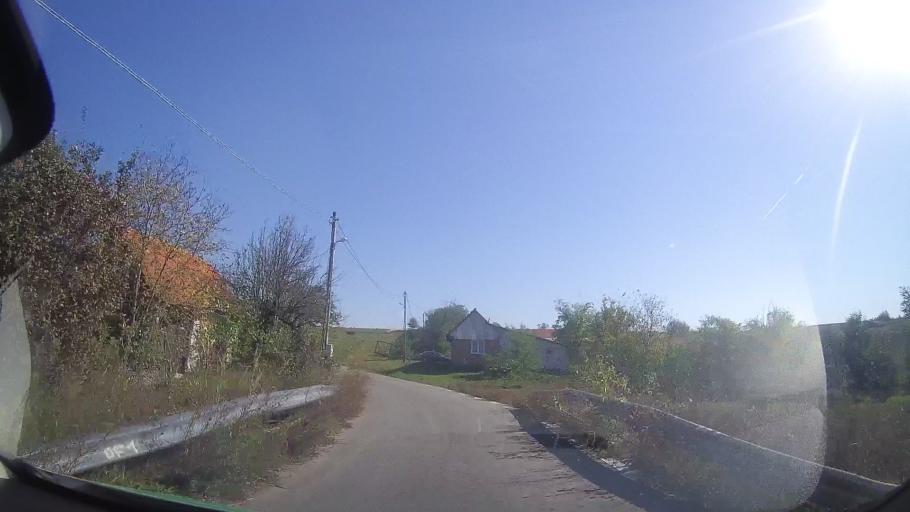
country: RO
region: Timis
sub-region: Comuna Ohaba Lunga
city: Ohaba Lunga
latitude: 45.9108
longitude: 21.9451
